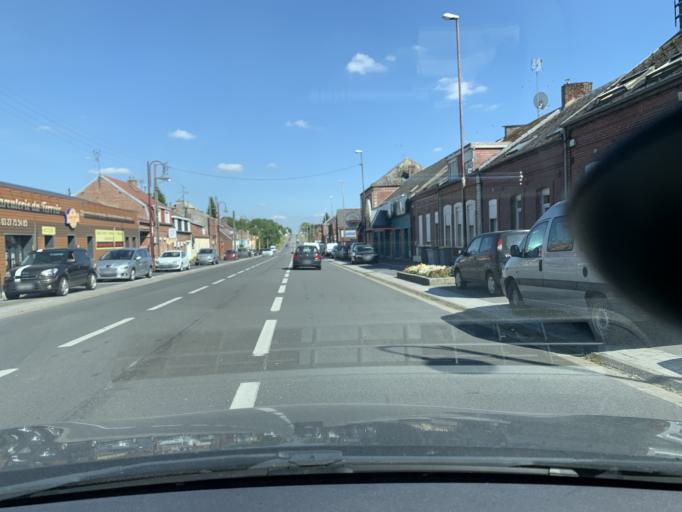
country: FR
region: Nord-Pas-de-Calais
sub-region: Departement du Nord
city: Beauvois-en-Cambresis
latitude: 50.1403
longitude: 3.3847
